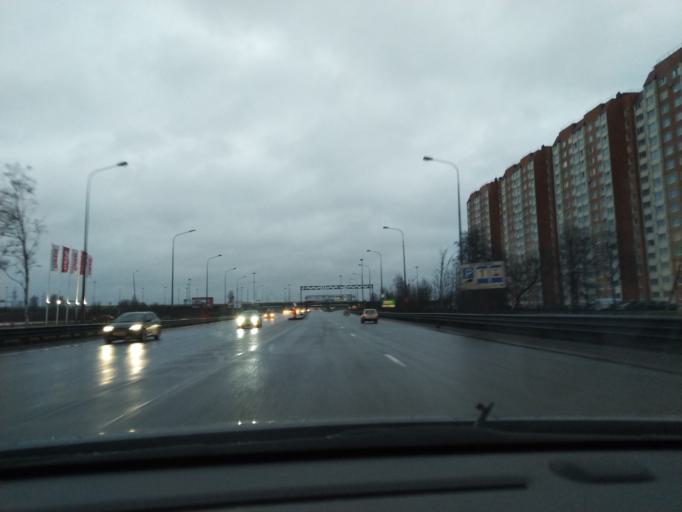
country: RU
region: St.-Petersburg
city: Gorelovo
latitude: 59.7944
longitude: 30.1502
